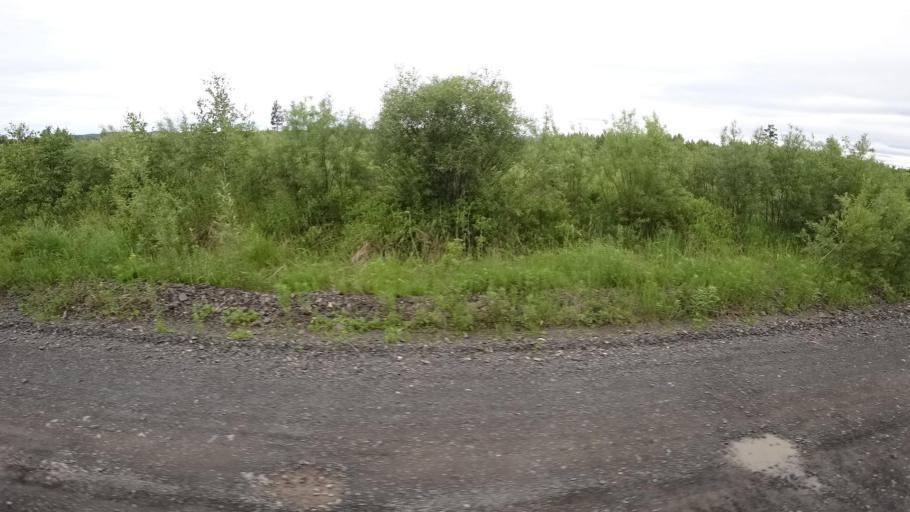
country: RU
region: Khabarovsk Krai
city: Amursk
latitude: 49.9077
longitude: 136.1480
